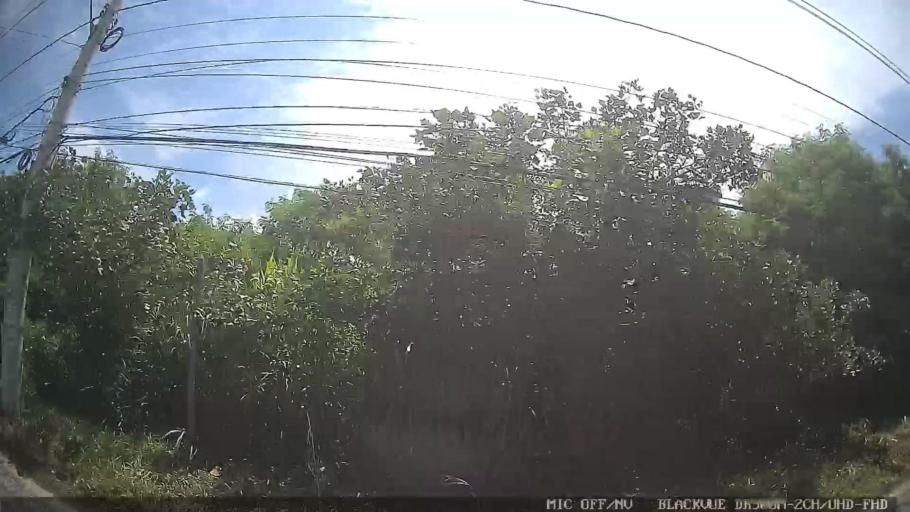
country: BR
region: Sao Paulo
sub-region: Santa Isabel
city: Santa Isabel
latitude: -23.3392
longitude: -46.2133
